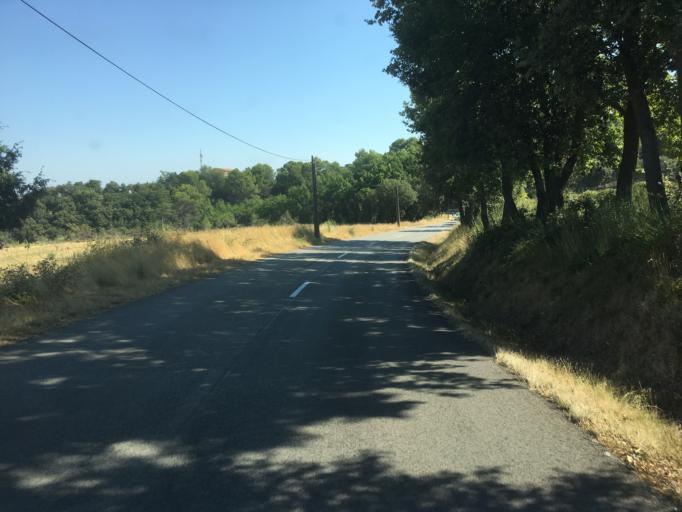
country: FR
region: Provence-Alpes-Cote d'Azur
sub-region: Departement des Alpes-de-Haute-Provence
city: Volx
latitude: 43.8345
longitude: 5.8660
